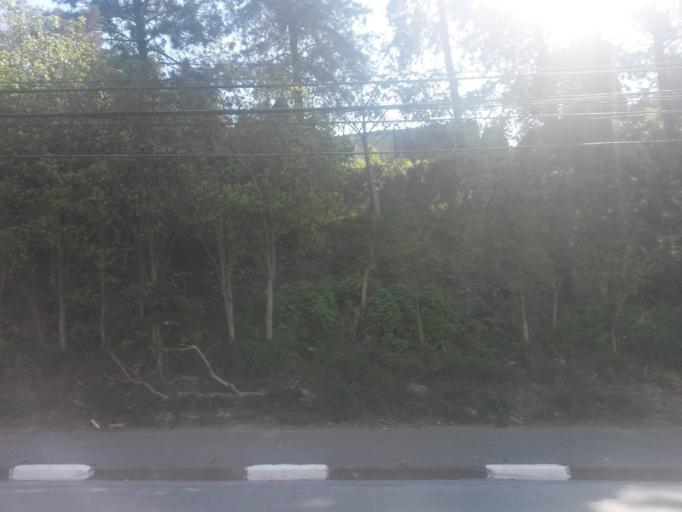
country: BR
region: Sao Paulo
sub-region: Sao Bernardo Do Campo
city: Sao Bernardo do Campo
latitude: -23.7436
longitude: -46.5246
